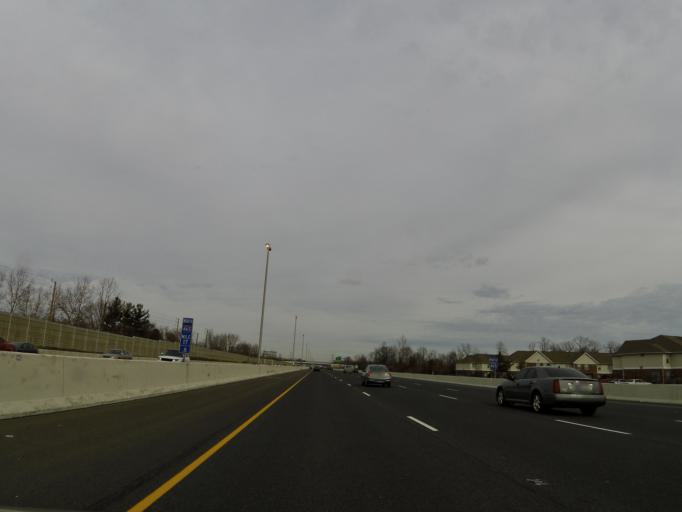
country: US
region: Indiana
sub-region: Marion County
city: Speedway
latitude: 39.8314
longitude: -86.2758
